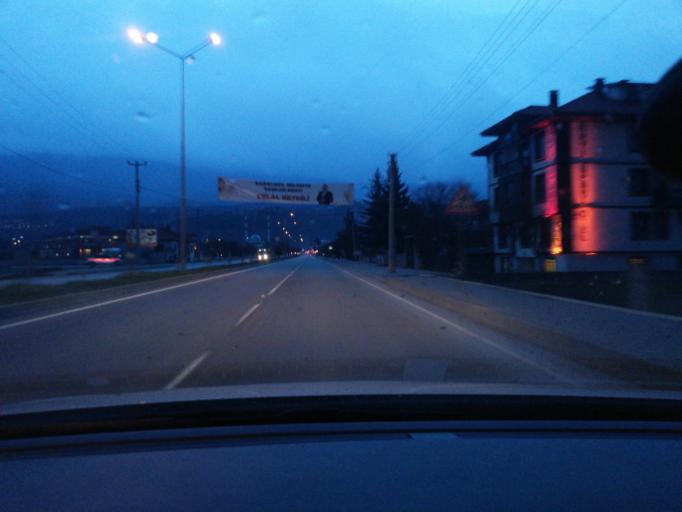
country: TR
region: Bolu
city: Bolu
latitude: 40.6944
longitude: 31.6192
